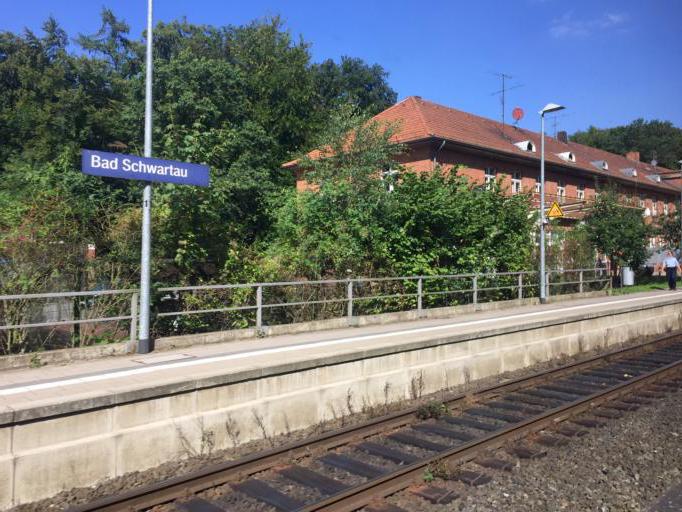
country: DE
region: Schleswig-Holstein
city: Bad Schwartau
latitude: 53.9159
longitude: 10.7023
